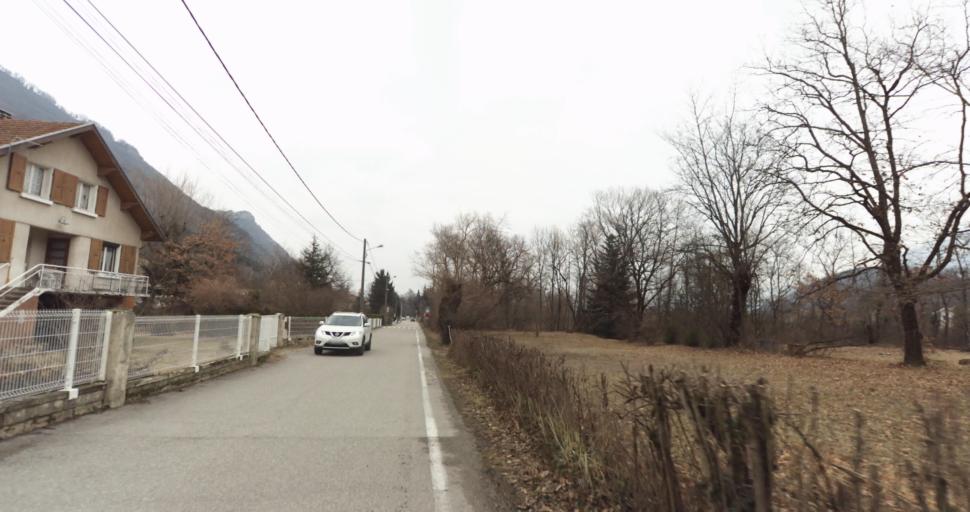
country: FR
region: Rhone-Alpes
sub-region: Departement de l'Isere
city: Vif
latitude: 45.0458
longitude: 5.6600
